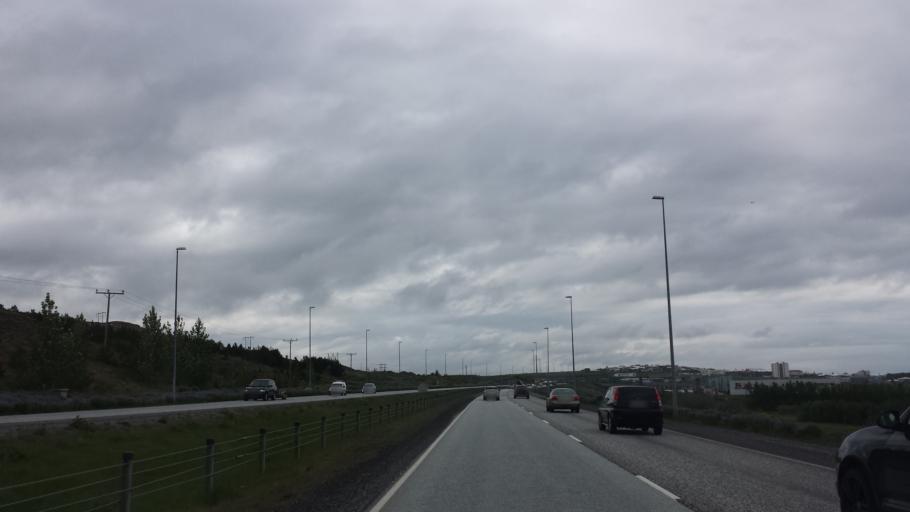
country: IS
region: Capital Region
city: Mosfellsbaer
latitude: 64.1509
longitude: -21.7414
